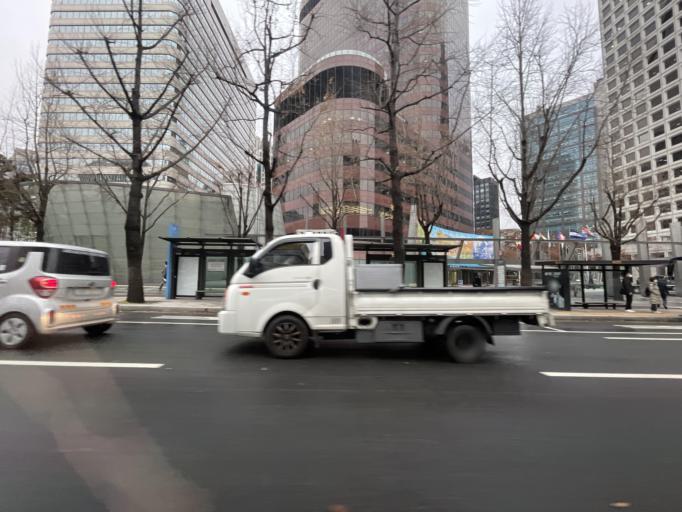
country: KR
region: Seoul
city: Seoul
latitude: 37.5613
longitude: 126.9759
